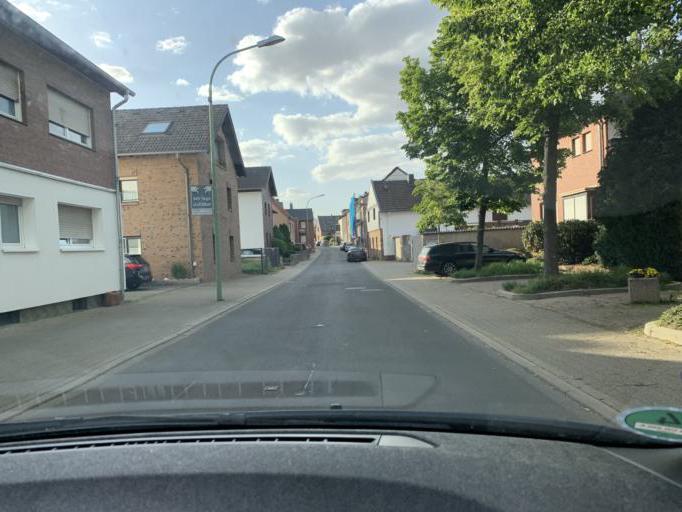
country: DE
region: North Rhine-Westphalia
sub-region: Regierungsbezirk Koln
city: Kreuzau
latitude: 50.7615
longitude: 6.4603
